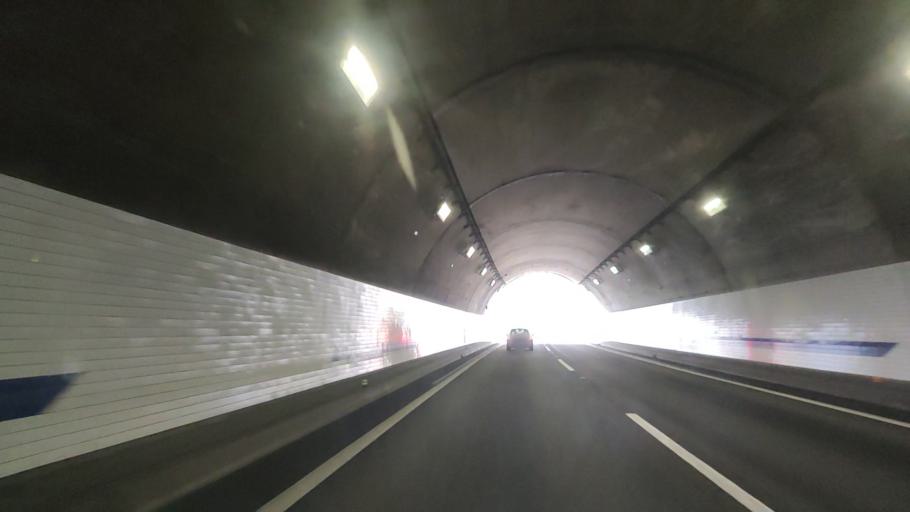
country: JP
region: Tokushima
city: Ishii
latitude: 34.1758
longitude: 134.4462
